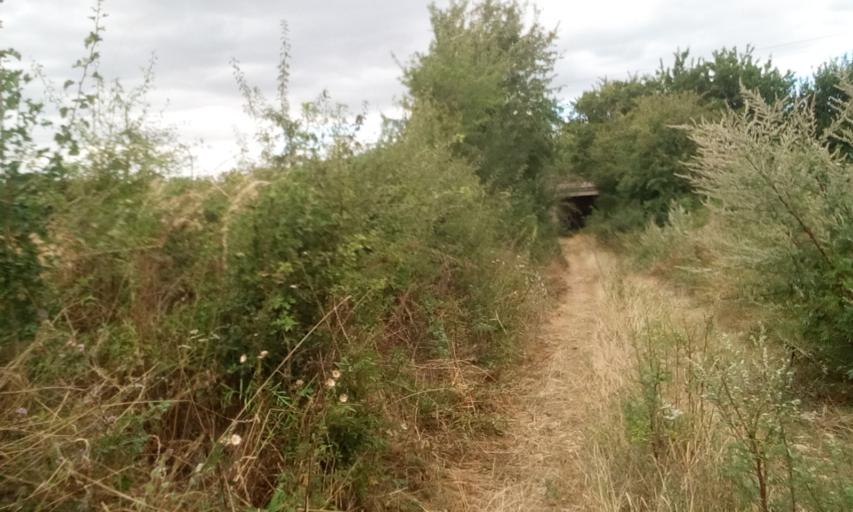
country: FR
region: Lower Normandy
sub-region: Departement du Calvados
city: Bellengreville
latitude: 49.1255
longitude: -0.2231
